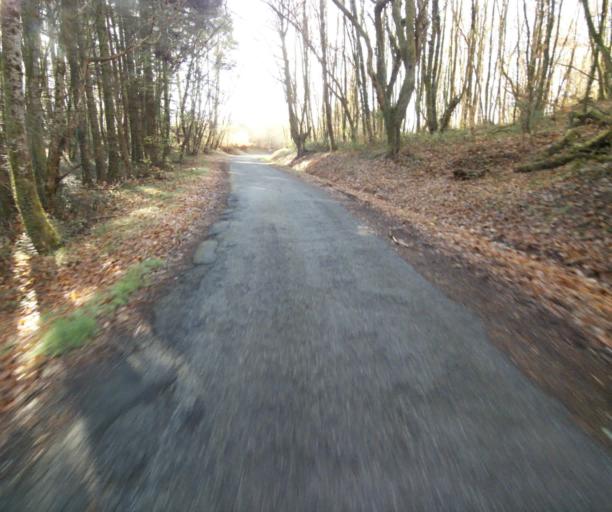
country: FR
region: Limousin
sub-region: Departement de la Correze
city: Laguenne
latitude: 45.2767
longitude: 1.8623
